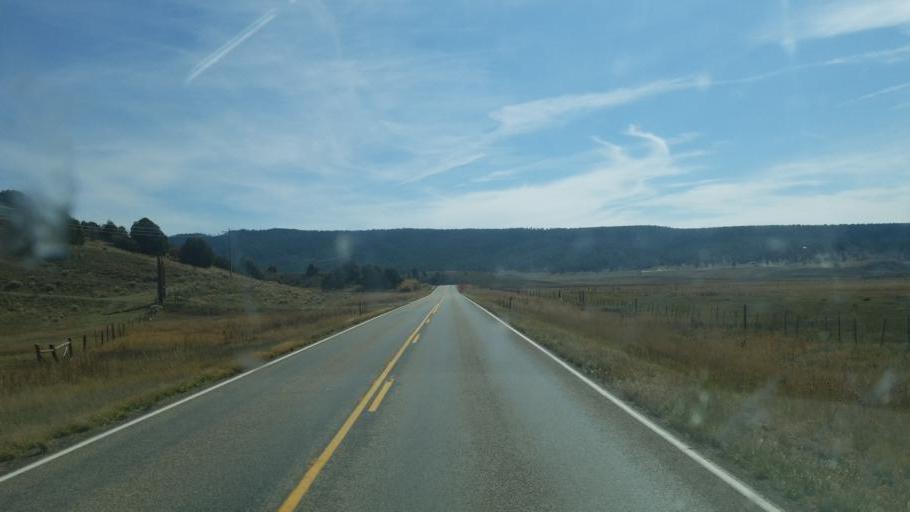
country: US
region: New Mexico
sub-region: Rio Arriba County
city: Dulce
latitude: 37.0865
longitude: -106.9006
